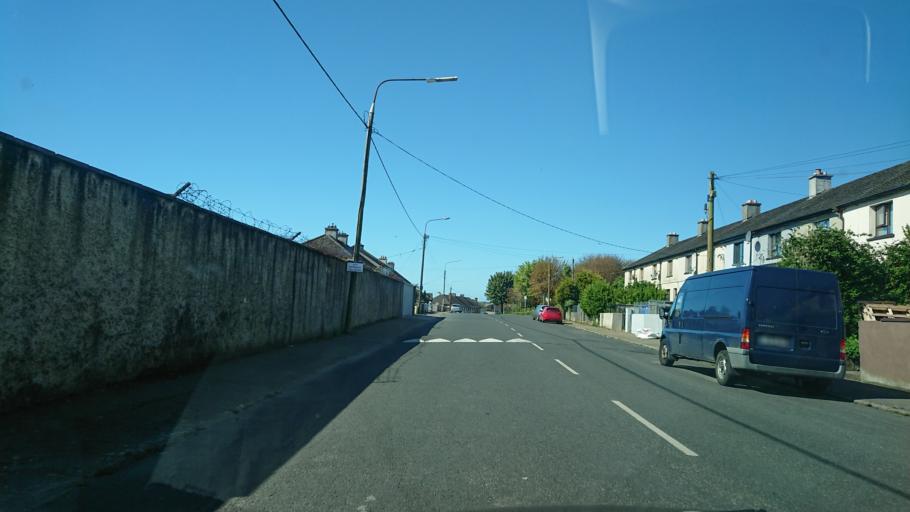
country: IE
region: Munster
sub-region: Waterford
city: Waterford
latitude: 52.2528
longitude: -7.1211
